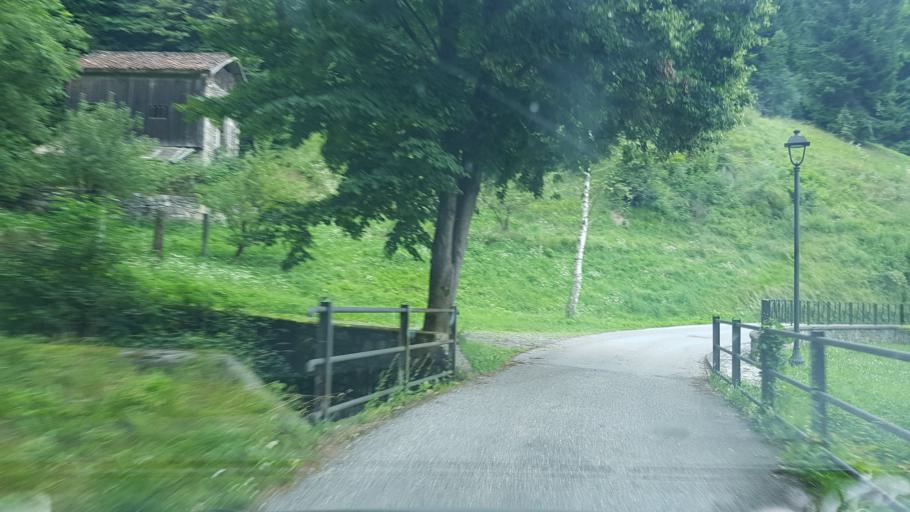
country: IT
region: Friuli Venezia Giulia
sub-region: Provincia di Udine
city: Cercivento
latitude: 46.5294
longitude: 12.9865
